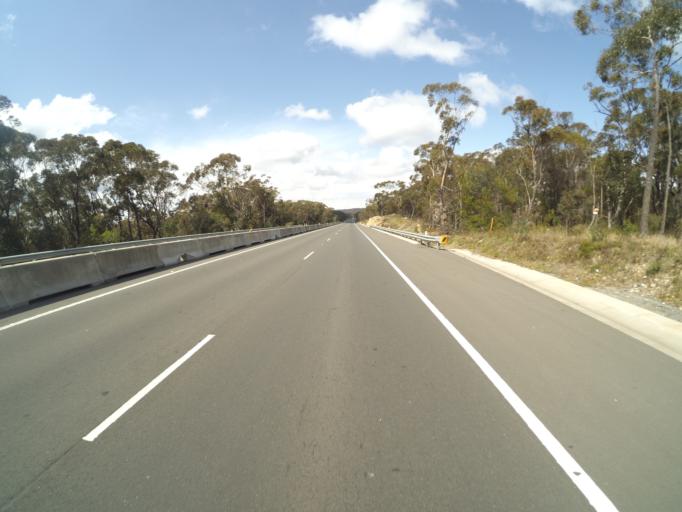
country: AU
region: New South Wales
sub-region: Wollongong
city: Mount Keira
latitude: -34.3632
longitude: 150.8225
